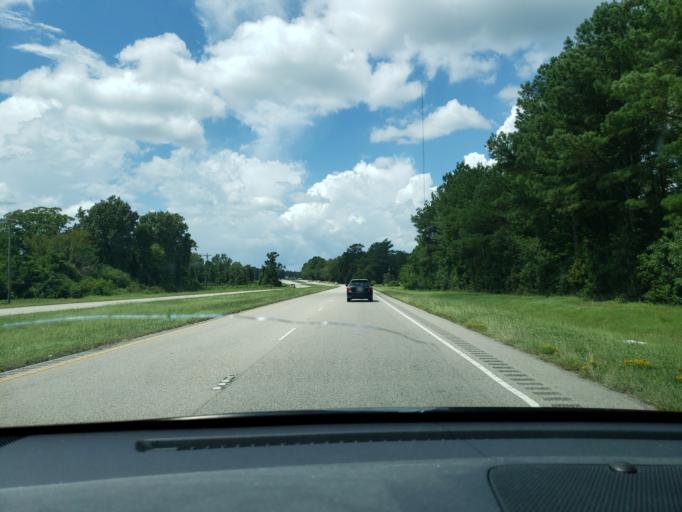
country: US
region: North Carolina
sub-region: Bladen County
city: Bladenboro
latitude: 34.7285
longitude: -78.7761
